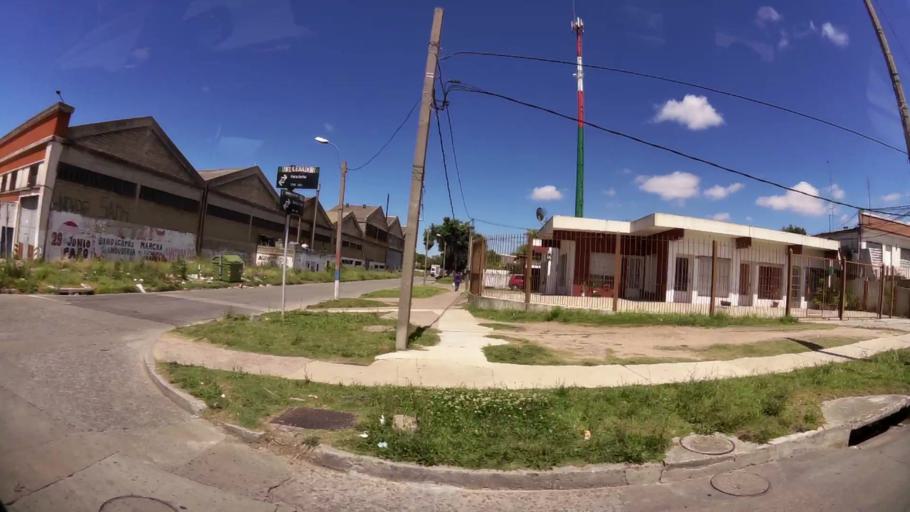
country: UY
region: Canelones
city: Paso de Carrasco
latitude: -34.8668
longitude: -56.1204
